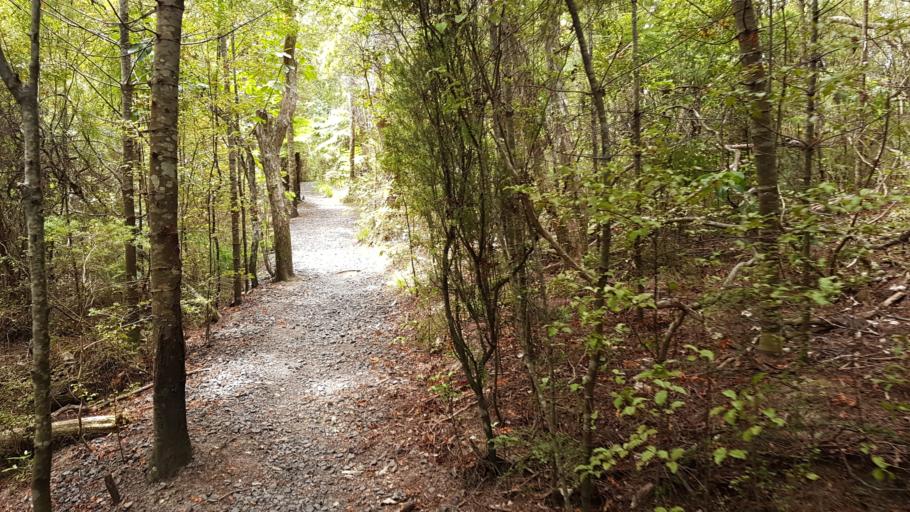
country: NZ
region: Auckland
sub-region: Auckland
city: North Shore
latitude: -36.8226
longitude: 174.7107
